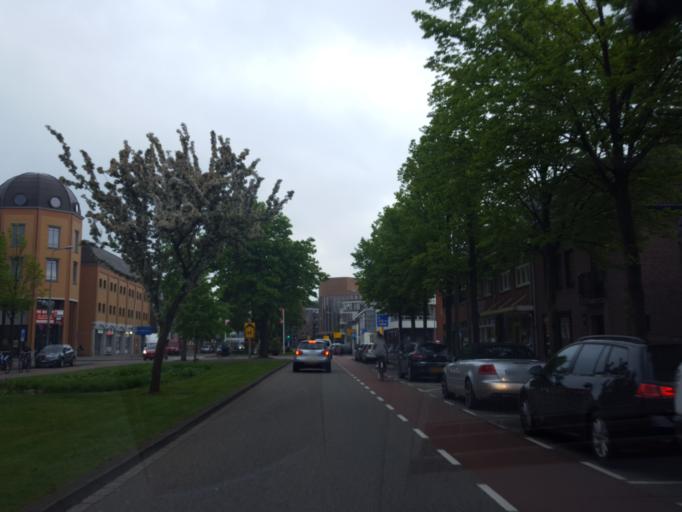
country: NL
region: Limburg
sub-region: Gemeente Weert
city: Weert
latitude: 51.2533
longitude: 5.7035
